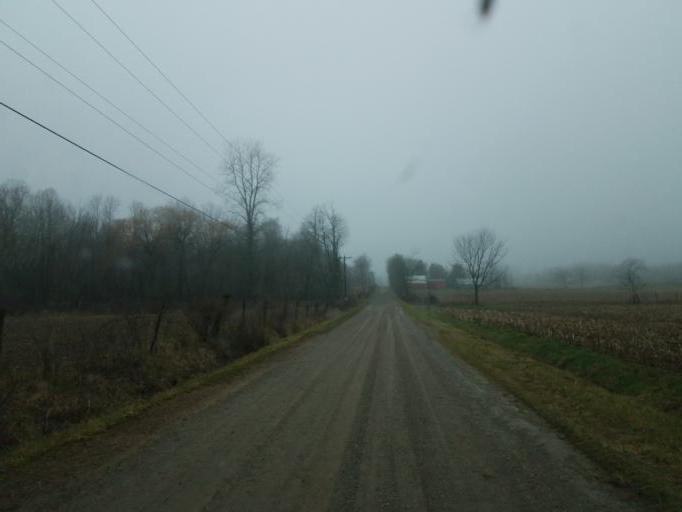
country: US
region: Ohio
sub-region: Richland County
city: Lexington
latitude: 40.6736
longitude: -82.6496
